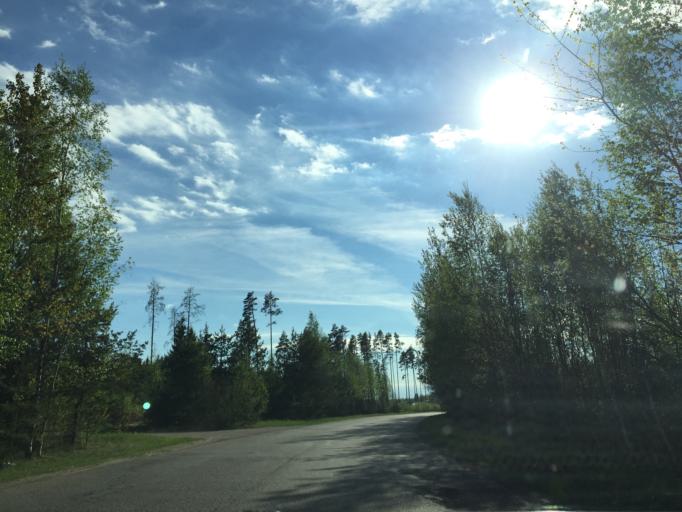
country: LV
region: Lecava
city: Iecava
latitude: 56.6911
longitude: 24.1033
